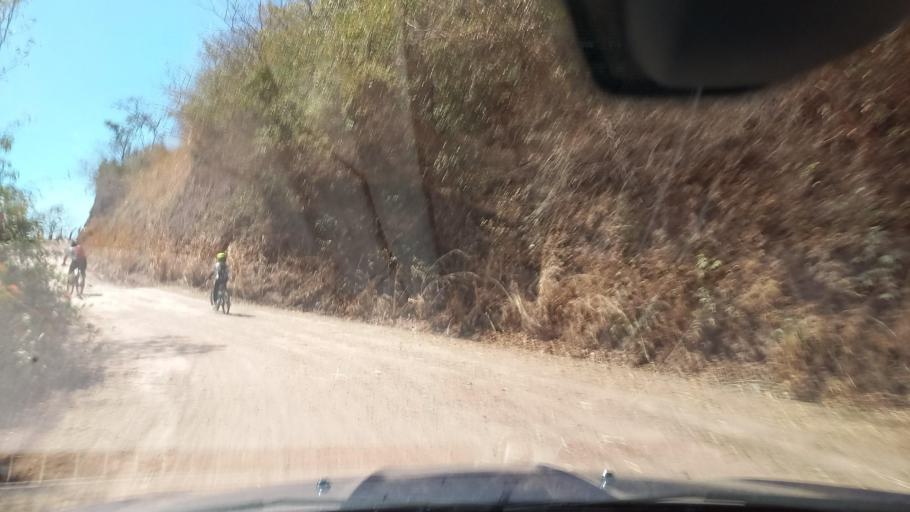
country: SV
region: Santa Ana
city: Metapan
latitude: 14.3670
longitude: -89.4966
